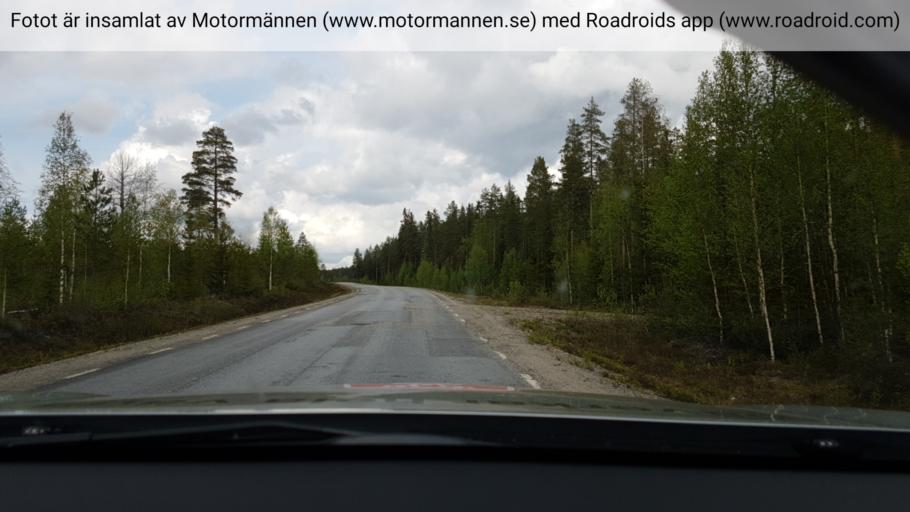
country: SE
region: Vaesternorrland
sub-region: OErnskoeldsviks Kommun
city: Bredbyn
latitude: 63.8996
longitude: 18.5032
